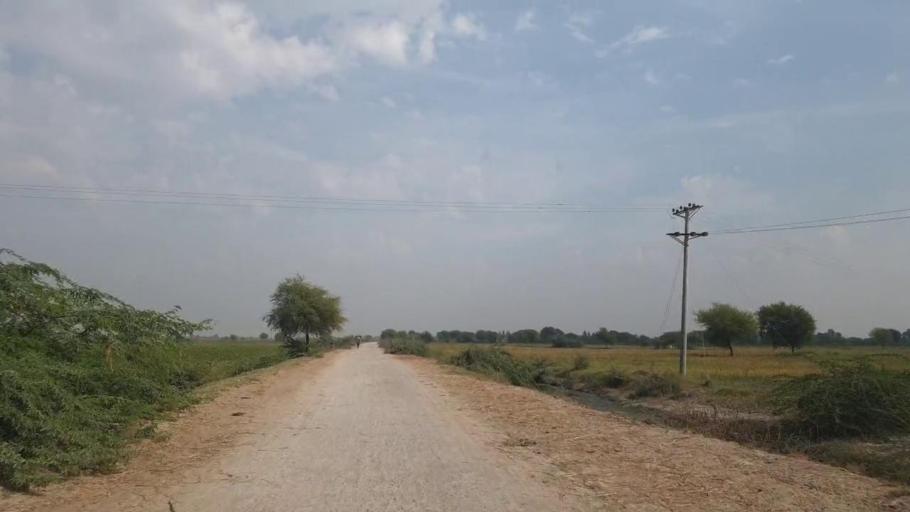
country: PK
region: Sindh
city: Rajo Khanani
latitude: 24.9570
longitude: 68.9915
